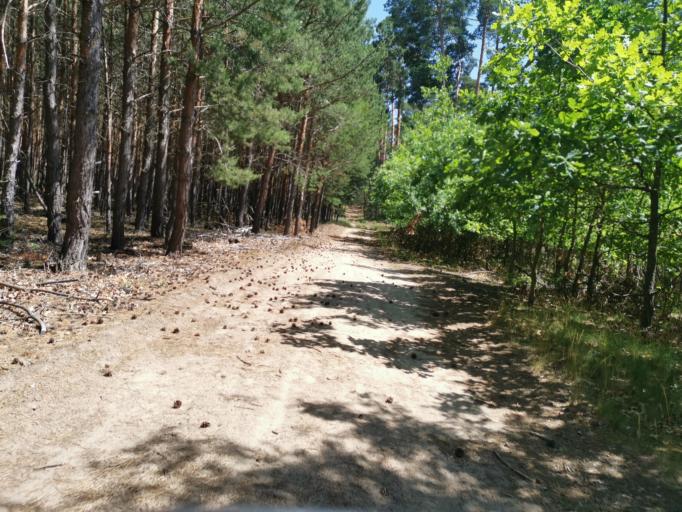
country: CZ
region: South Moravian
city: Bzenec
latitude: 48.9440
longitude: 17.2427
